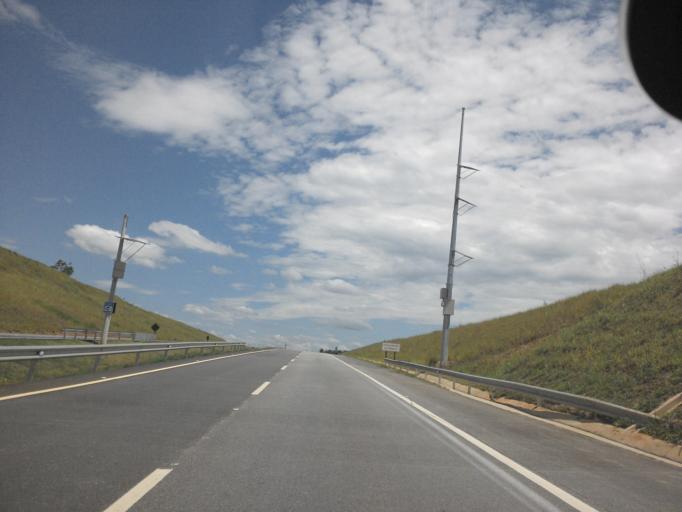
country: BR
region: Sao Paulo
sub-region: Taubate
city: Taubate
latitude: -23.0881
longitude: -45.5669
